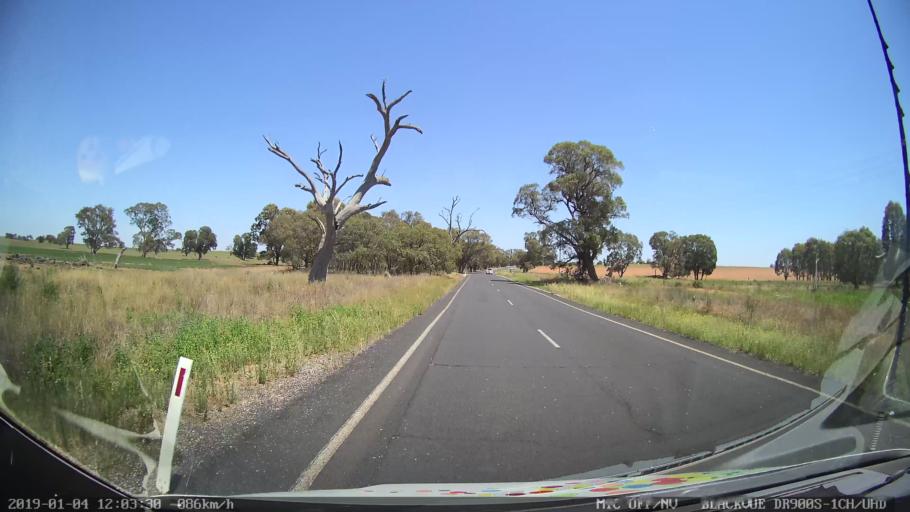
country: AU
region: New South Wales
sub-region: Wellington
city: Wellington
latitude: -32.7725
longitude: 148.6707
